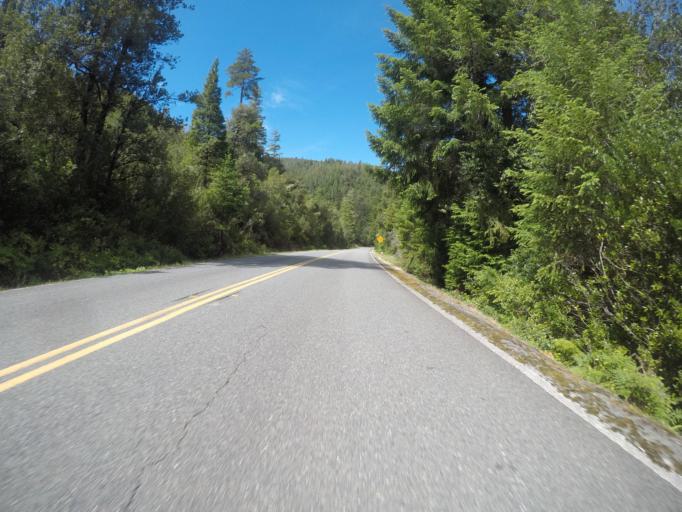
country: US
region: California
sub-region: Del Norte County
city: Bertsch-Oceanview
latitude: 41.7247
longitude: -123.9686
